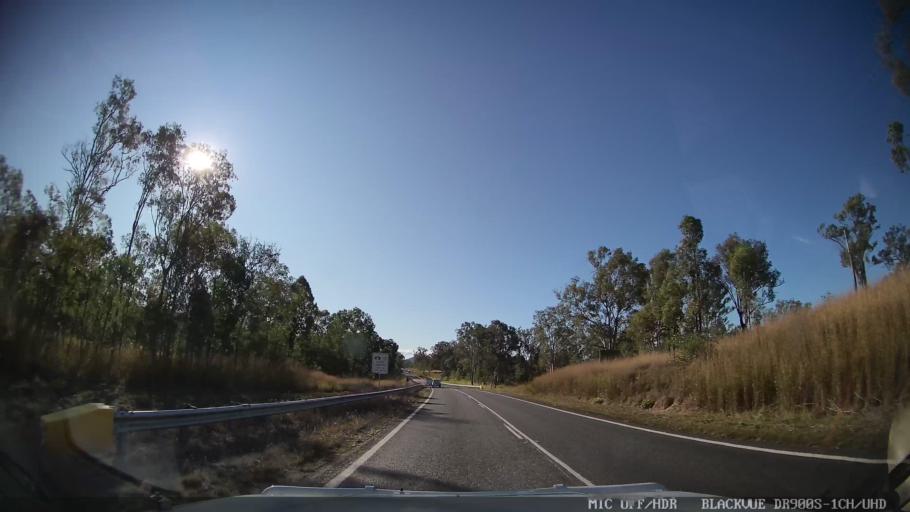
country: AU
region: Queensland
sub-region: Bundaberg
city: Sharon
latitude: -24.8303
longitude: 151.7087
